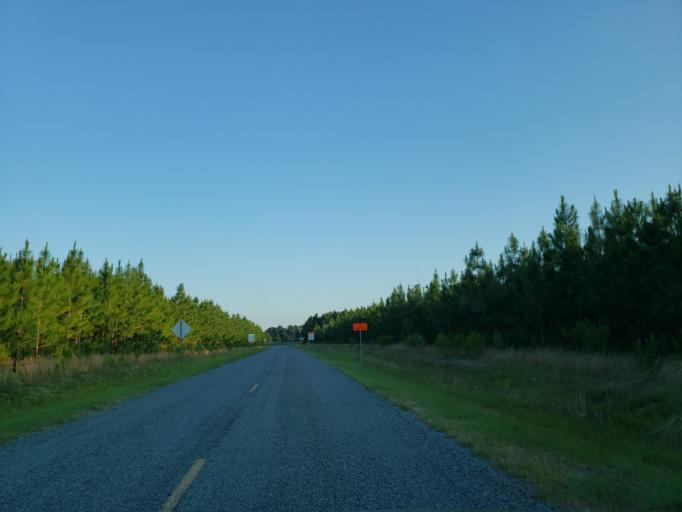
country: US
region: Georgia
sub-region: Dooly County
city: Vienna
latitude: 32.1094
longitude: -83.7557
